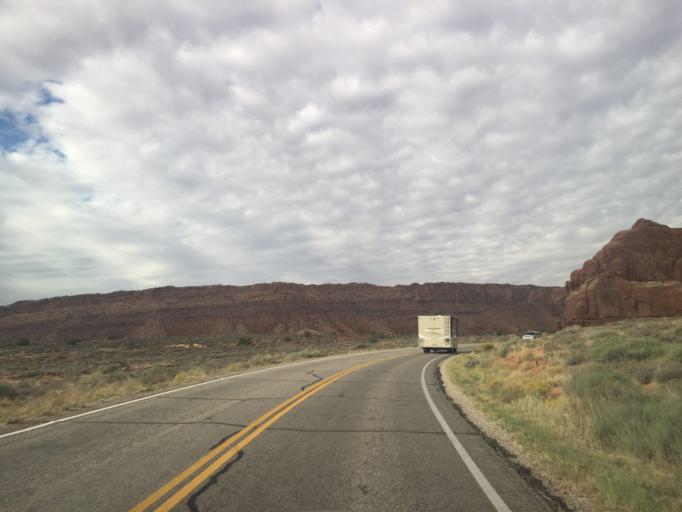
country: US
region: Utah
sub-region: Grand County
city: Moab
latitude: 38.6203
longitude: -109.6020
